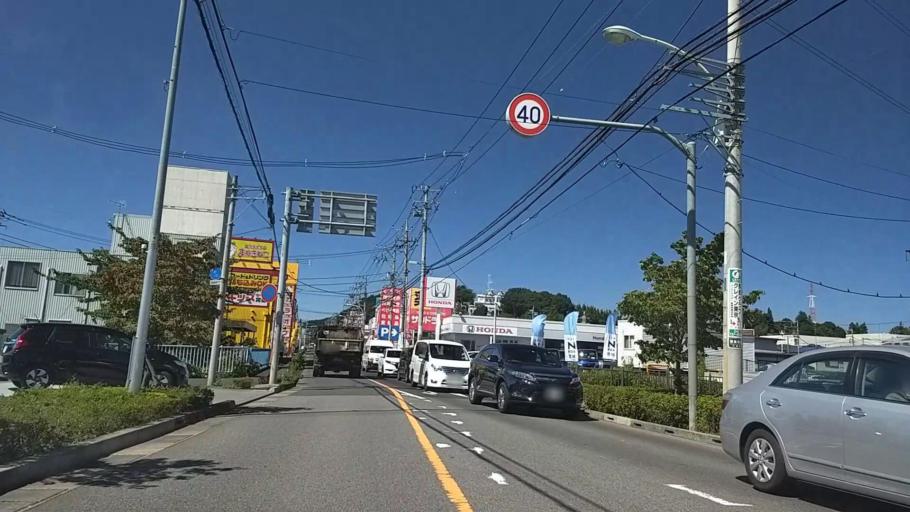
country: JP
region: Tokyo
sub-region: Machida-shi
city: Machida
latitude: 35.5888
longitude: 139.4597
